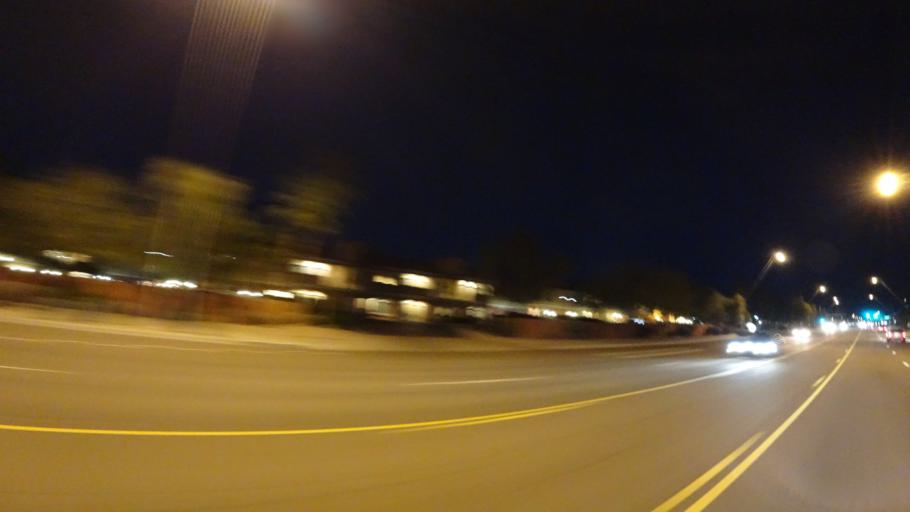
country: US
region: Arizona
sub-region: Maricopa County
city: Mesa
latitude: 33.4518
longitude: -111.6955
